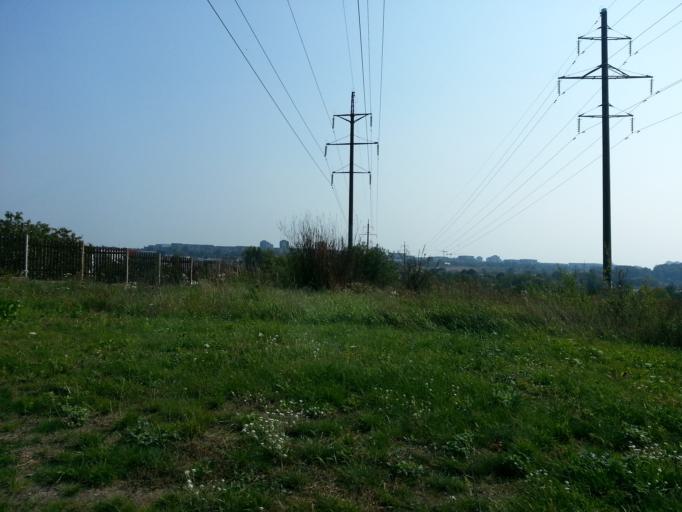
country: LT
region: Vilnius County
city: Justiniskes
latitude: 54.7264
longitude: 25.1956
